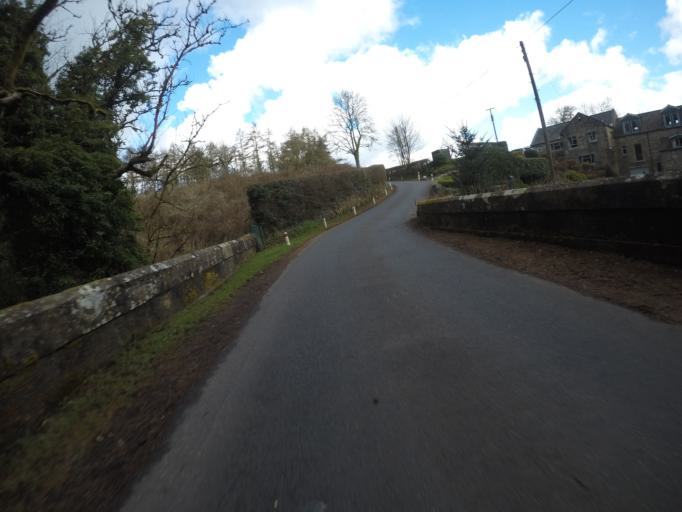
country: GB
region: Scotland
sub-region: North Ayrshire
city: Kilwinning
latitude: 55.6919
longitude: -4.6738
